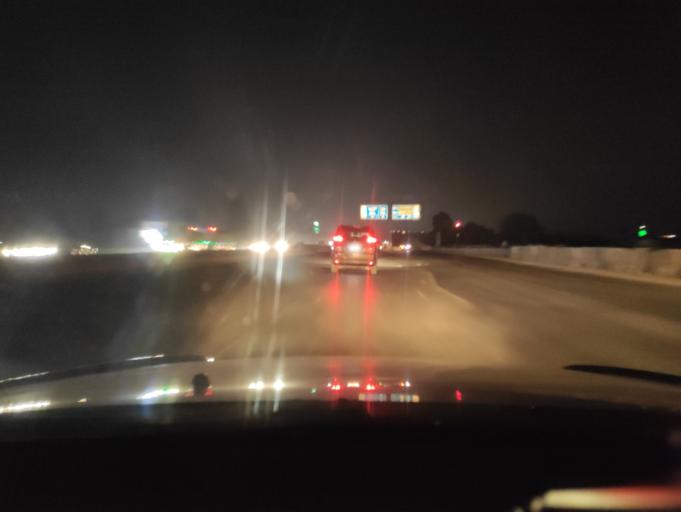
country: EG
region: Muhafazat al Qalyubiyah
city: Banha
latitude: 30.5013
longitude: 31.1641
